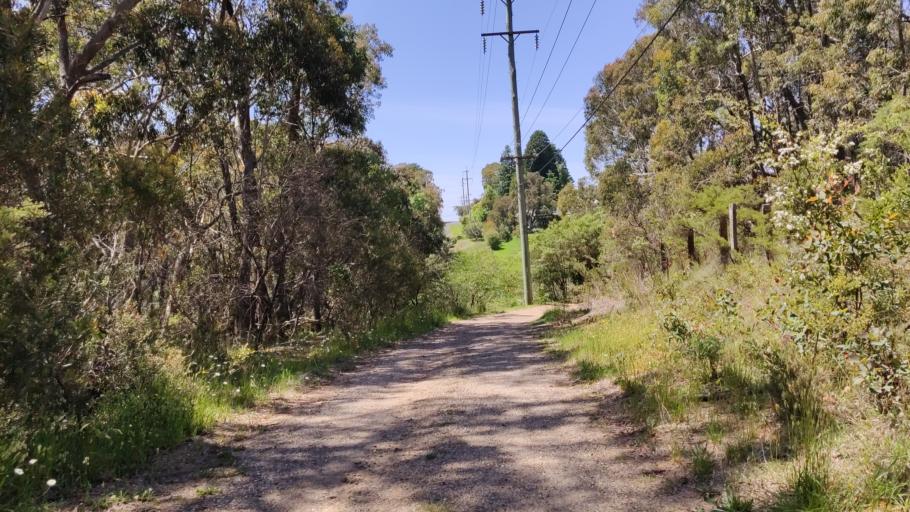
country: AU
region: New South Wales
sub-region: Blue Mountains Municipality
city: Blackheath
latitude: -33.6280
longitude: 150.2884
